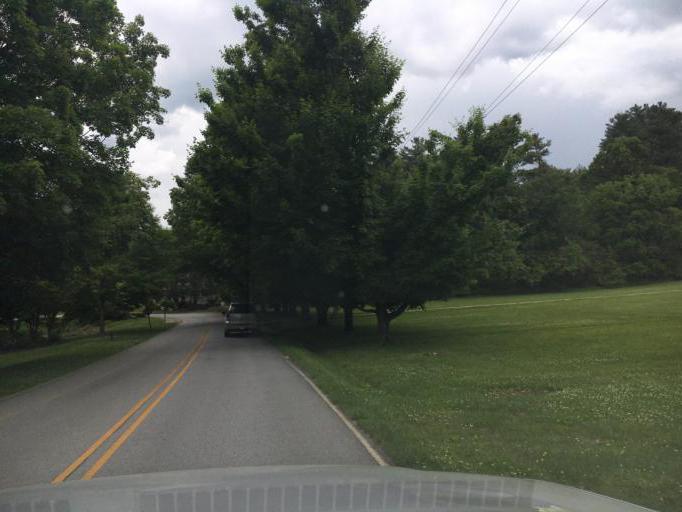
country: US
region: North Carolina
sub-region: Transylvania County
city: Brevard
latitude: 35.2487
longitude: -82.7252
